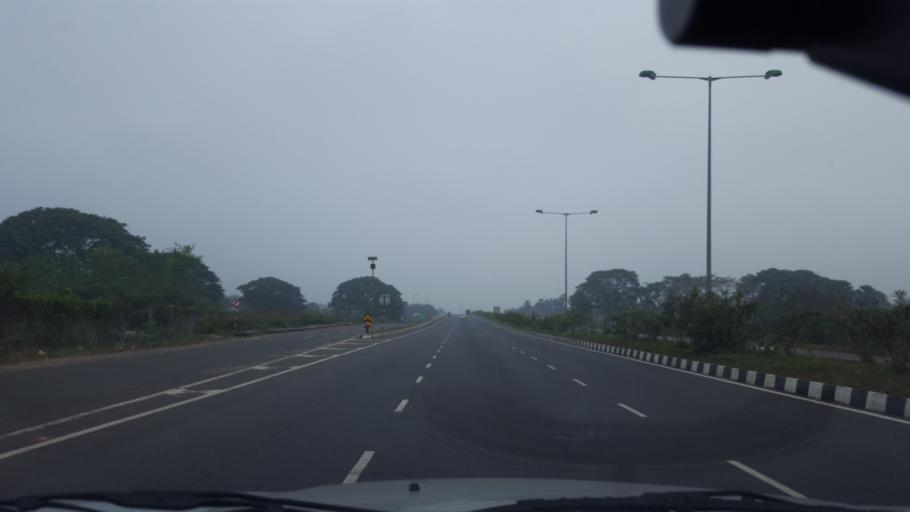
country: IN
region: Andhra Pradesh
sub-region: Prakasam
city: Addanki
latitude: 15.8188
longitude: 80.0433
